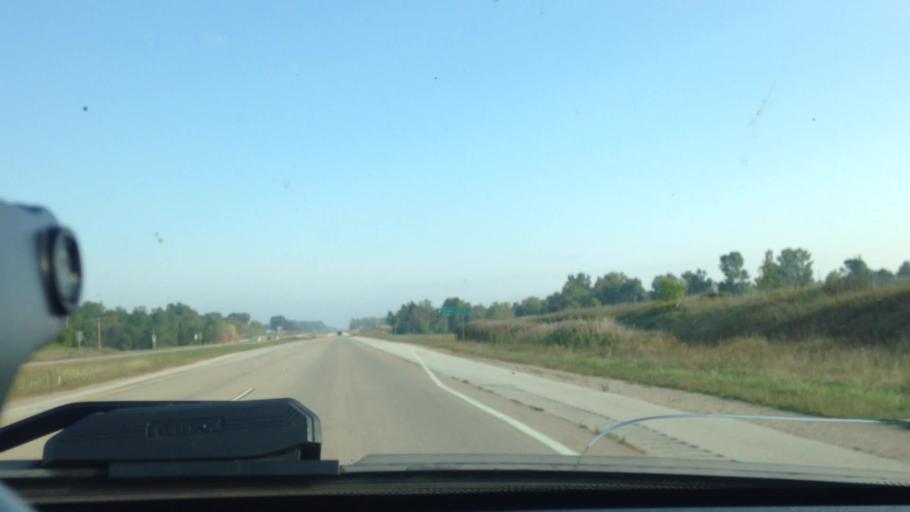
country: US
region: Wisconsin
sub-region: Oconto County
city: Oconto Falls
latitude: 45.0064
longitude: -88.0450
